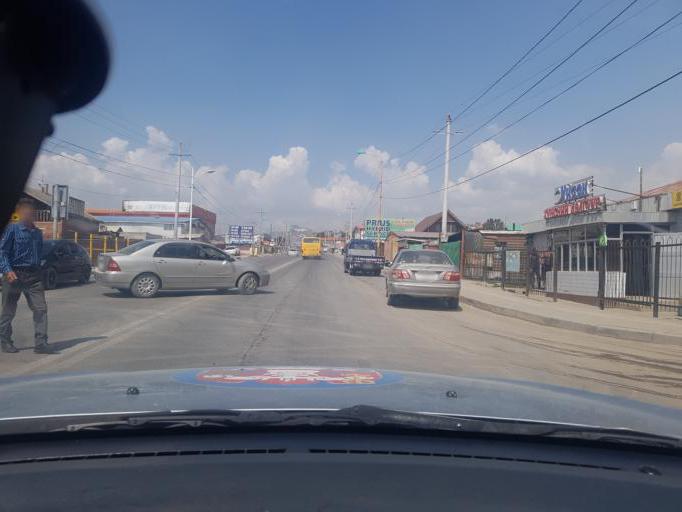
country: MN
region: Ulaanbaatar
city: Ulaanbaatar
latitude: 47.9313
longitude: 106.8880
